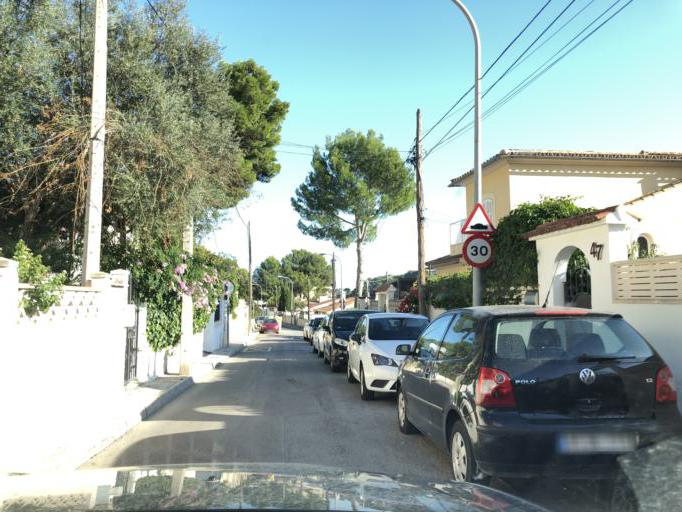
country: ES
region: Balearic Islands
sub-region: Illes Balears
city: Camp de Mar
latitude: 39.5397
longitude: 2.4409
